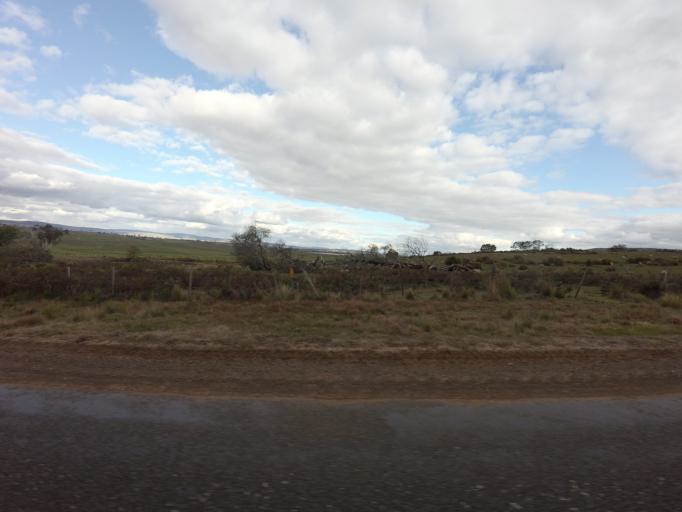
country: AU
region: Tasmania
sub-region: Northern Midlands
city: Evandale
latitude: -41.8943
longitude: 147.4128
